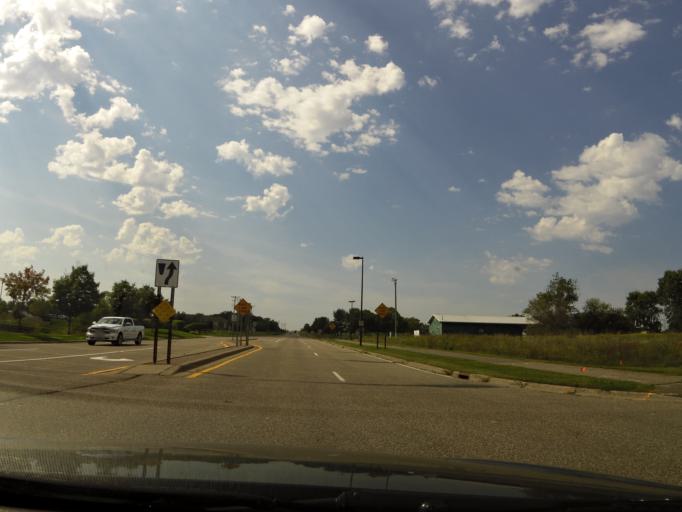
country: US
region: Minnesota
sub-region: Washington County
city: Oakdale
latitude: 44.9525
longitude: -92.9370
